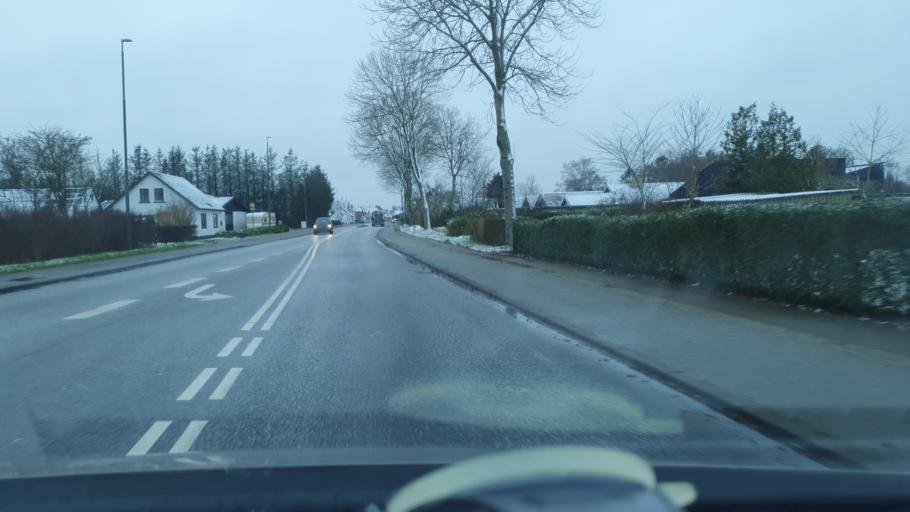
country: DK
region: North Denmark
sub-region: Jammerbugt Kommune
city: Brovst
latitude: 57.1118
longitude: 9.5938
